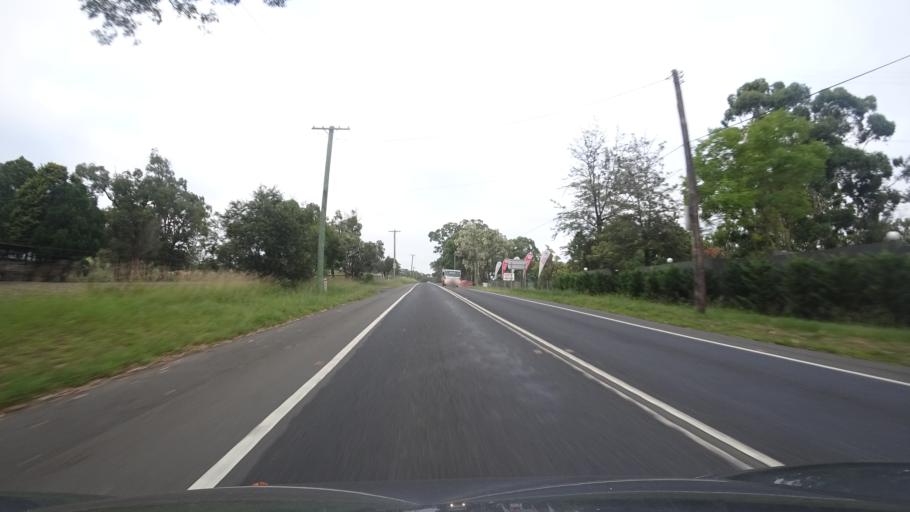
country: AU
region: New South Wales
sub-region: Blacktown
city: Rouse Hill
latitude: -33.6587
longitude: 150.9270
